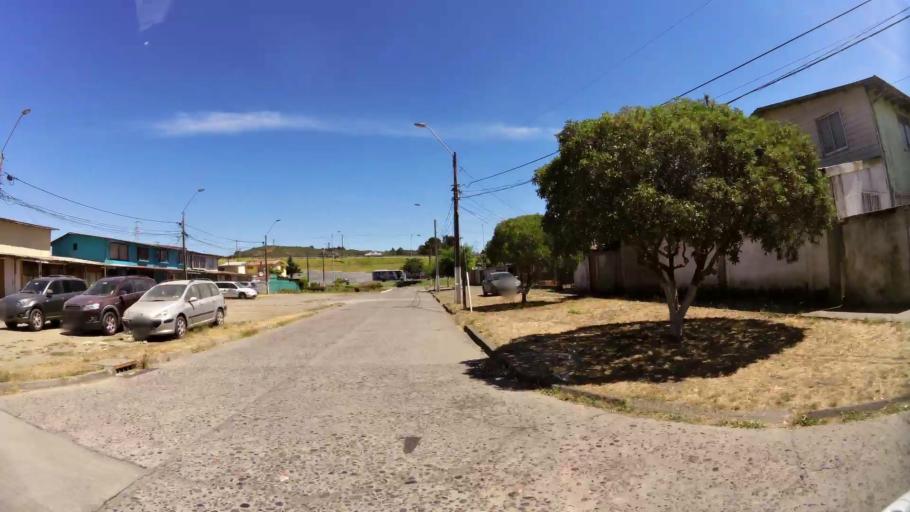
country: CL
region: Biobio
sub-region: Provincia de Concepcion
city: Talcahuano
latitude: -36.7644
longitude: -73.0854
